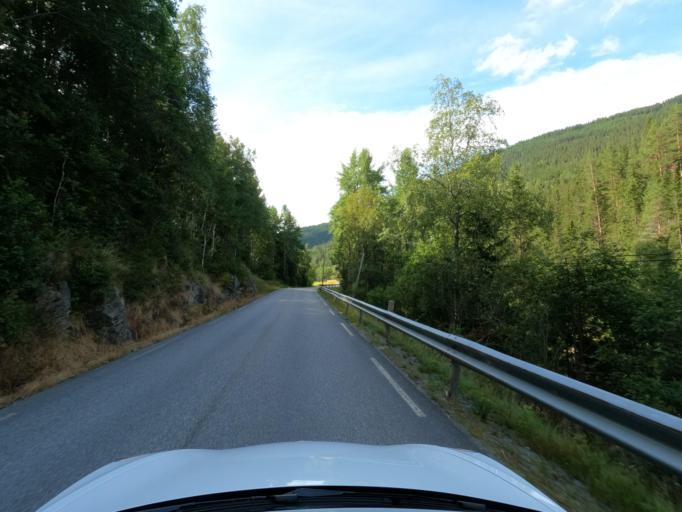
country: NO
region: Buskerud
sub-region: Nore og Uvdal
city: Rodberg
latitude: 60.0775
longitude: 8.7709
